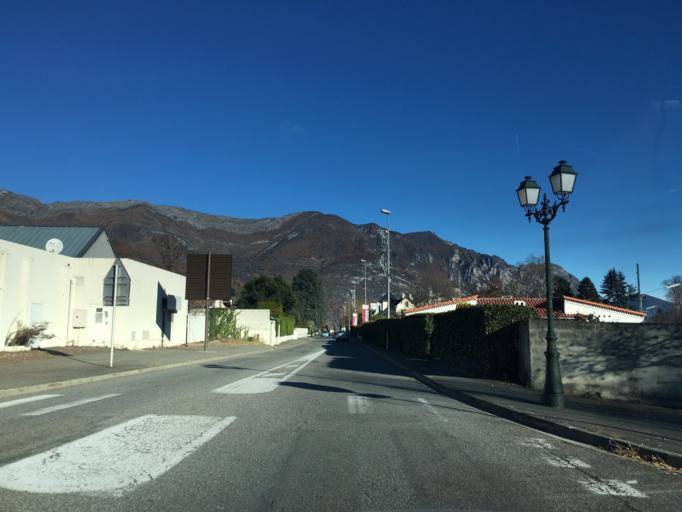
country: FR
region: Midi-Pyrenees
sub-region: Departement des Hautes-Pyrenees
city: Argeles-Gazost
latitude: 43.0020
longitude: -0.0991
